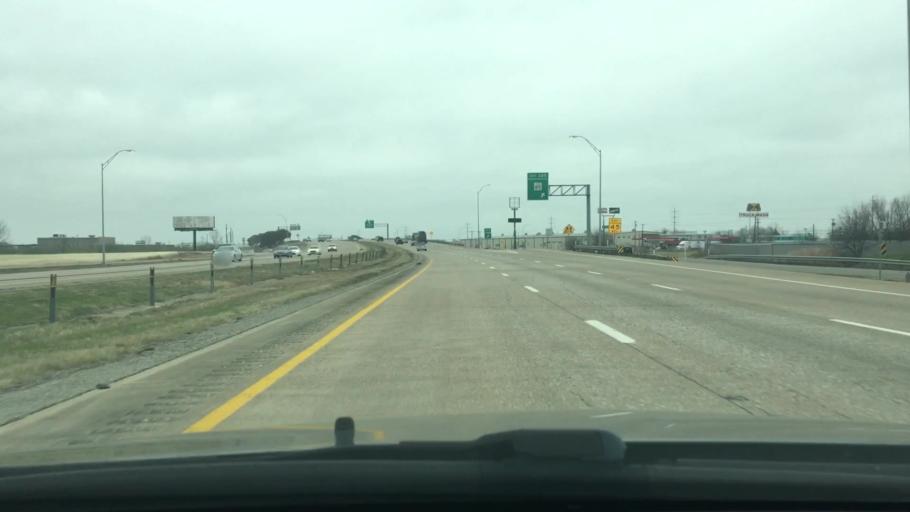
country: US
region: Texas
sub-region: Ellis County
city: Ennis
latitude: 32.3140
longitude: -96.6005
